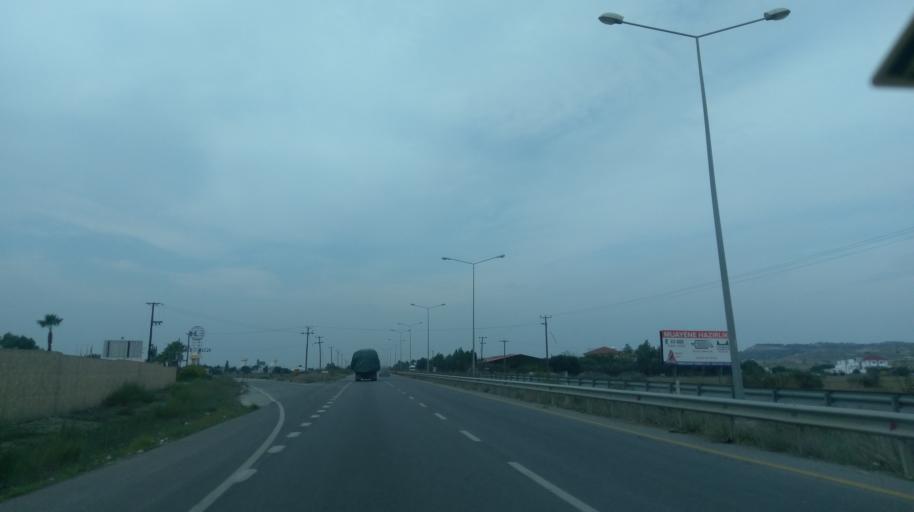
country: CY
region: Lefkosia
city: Mammari
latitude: 35.2114
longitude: 33.2367
